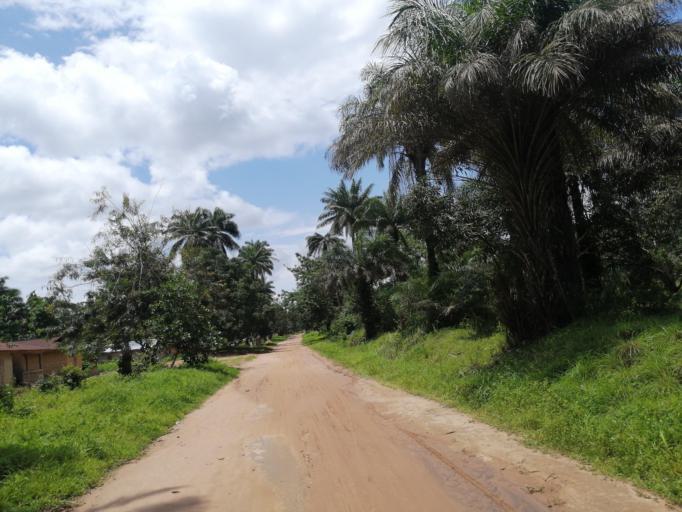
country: SL
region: Northern Province
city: Konakridee
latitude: 8.7722
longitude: -13.1386
